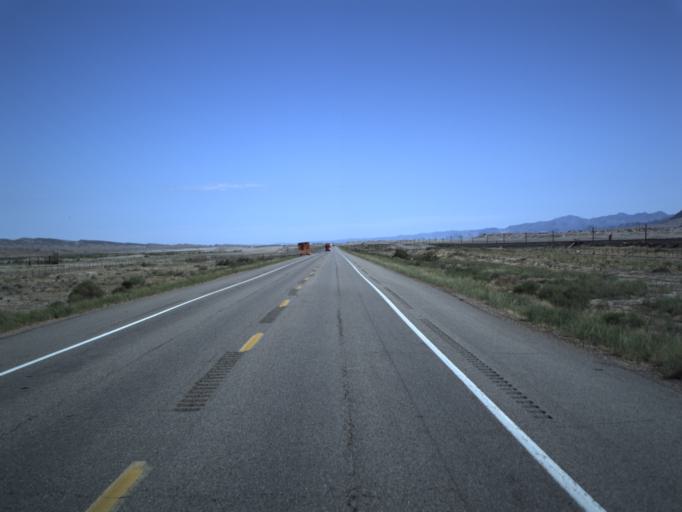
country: US
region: Utah
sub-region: Carbon County
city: East Carbon City
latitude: 39.0996
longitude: -110.3233
